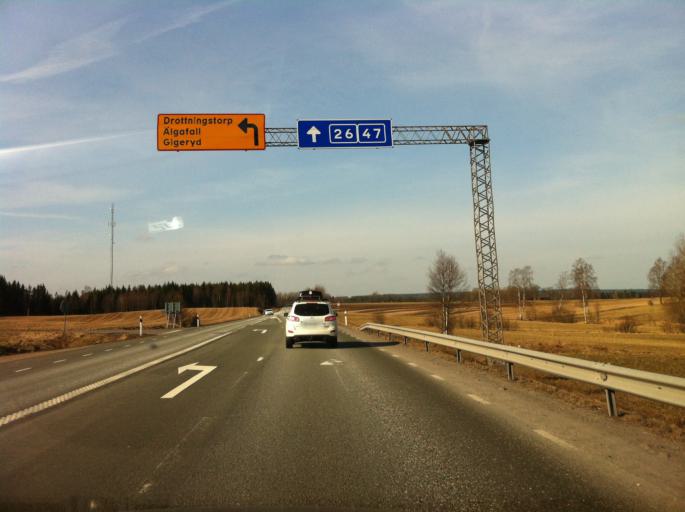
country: SE
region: Joenkoeping
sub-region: Habo Kommun
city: Habo
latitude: 57.8560
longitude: 14.0179
